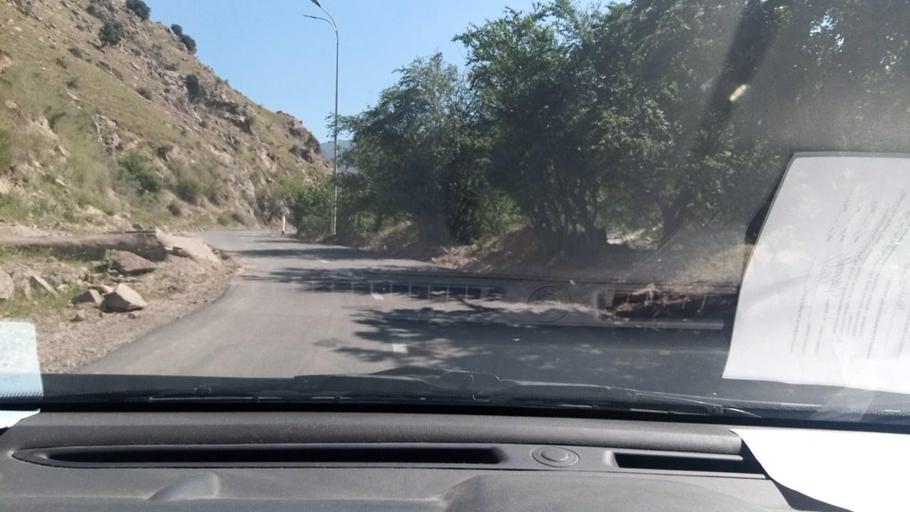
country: UZ
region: Toshkent
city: Yangiobod
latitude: 41.1230
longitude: 70.1038
